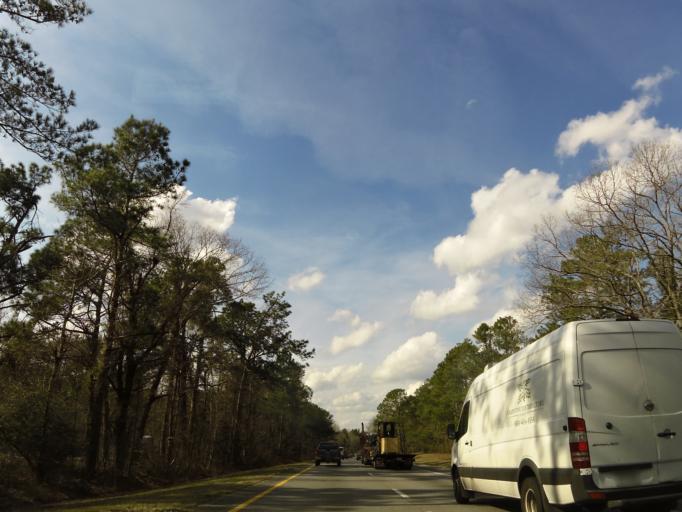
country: US
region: South Carolina
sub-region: Dorchester County
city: Ridgeville
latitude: 33.1549
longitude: -80.3465
